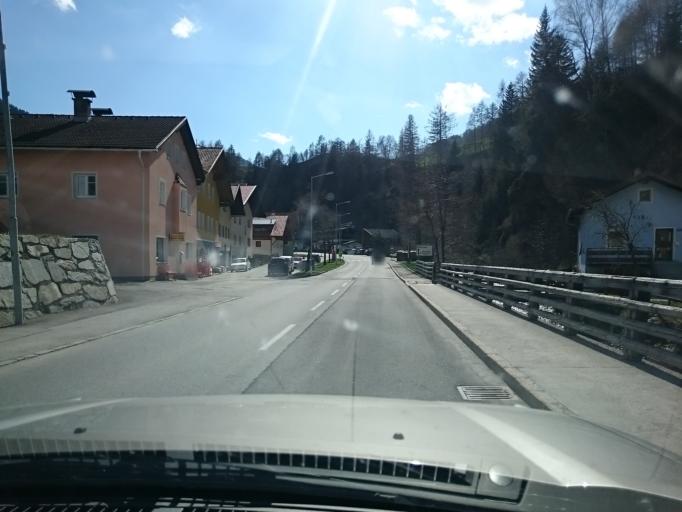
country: AT
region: Tyrol
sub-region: Politischer Bezirk Innsbruck Land
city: Gries am Brenner
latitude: 47.0396
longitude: 11.4807
